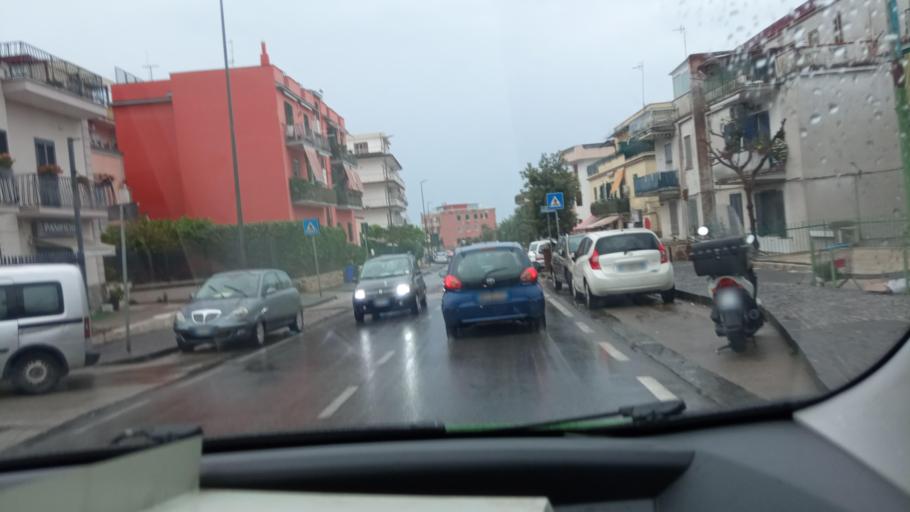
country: IT
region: Campania
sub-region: Provincia di Napoli
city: Pozzuoli
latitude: 40.8335
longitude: 14.1158
